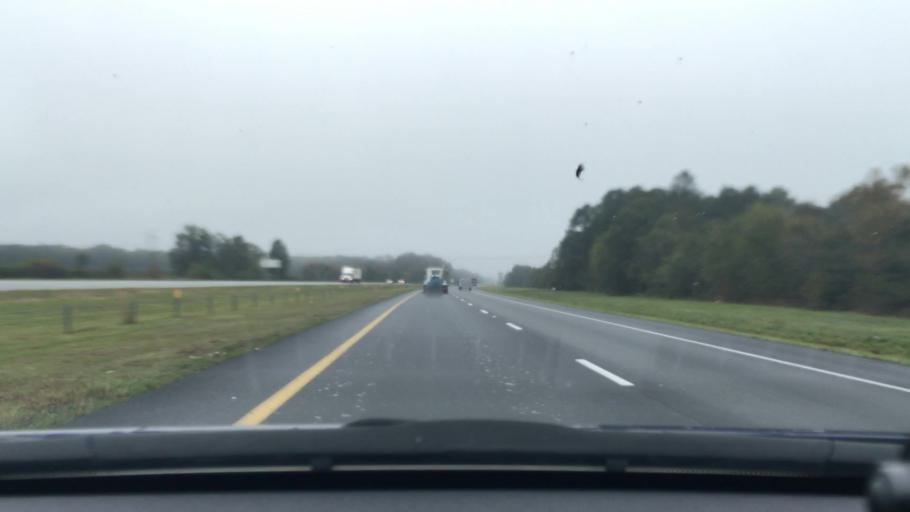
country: US
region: South Carolina
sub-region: Lee County
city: Bishopville
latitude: 34.1864
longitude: -80.2227
